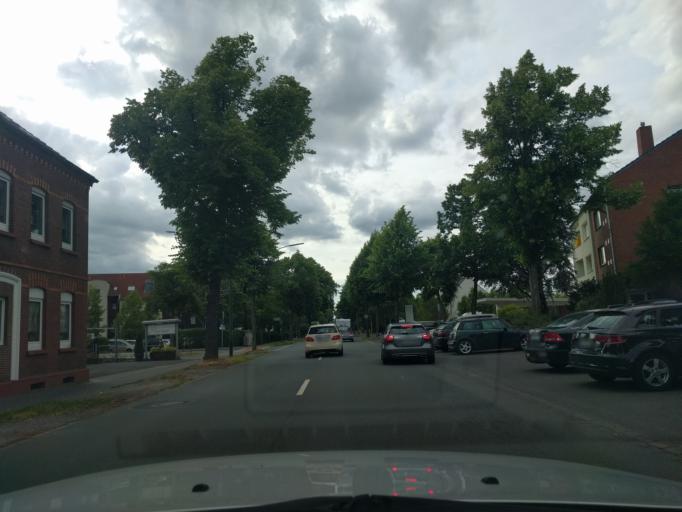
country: DE
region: North Rhine-Westphalia
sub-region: Regierungsbezirk Dusseldorf
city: Neuss
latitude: 51.2364
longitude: 6.7128
